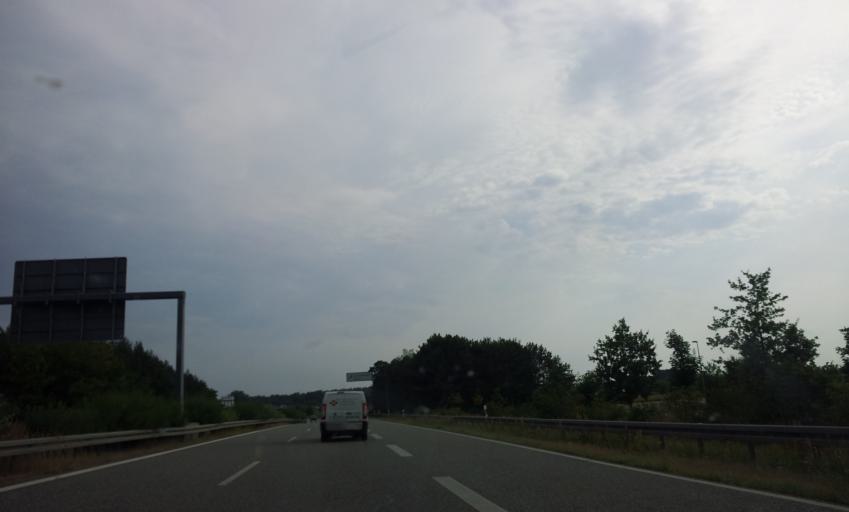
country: DE
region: Brandenburg
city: Ludwigsfelde
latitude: 52.2999
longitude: 13.2846
